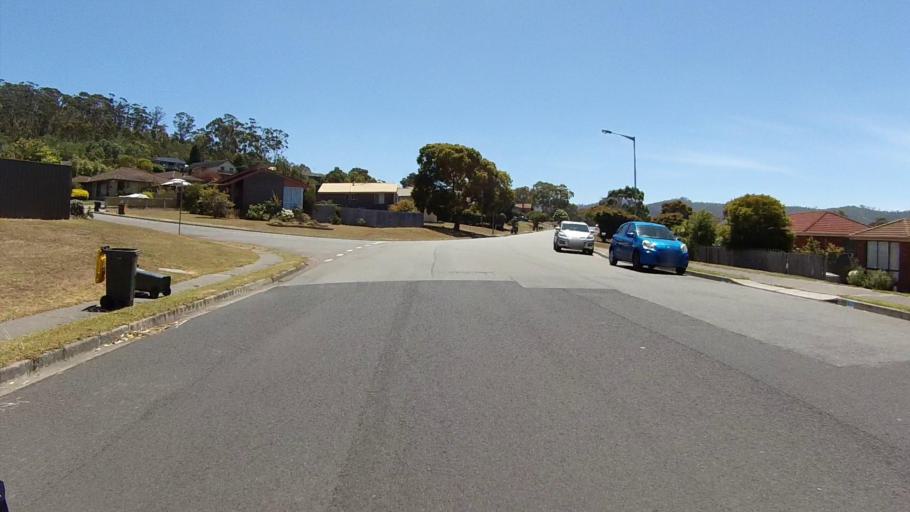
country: AU
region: Tasmania
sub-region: Clarence
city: Rokeby
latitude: -42.9031
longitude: 147.4283
